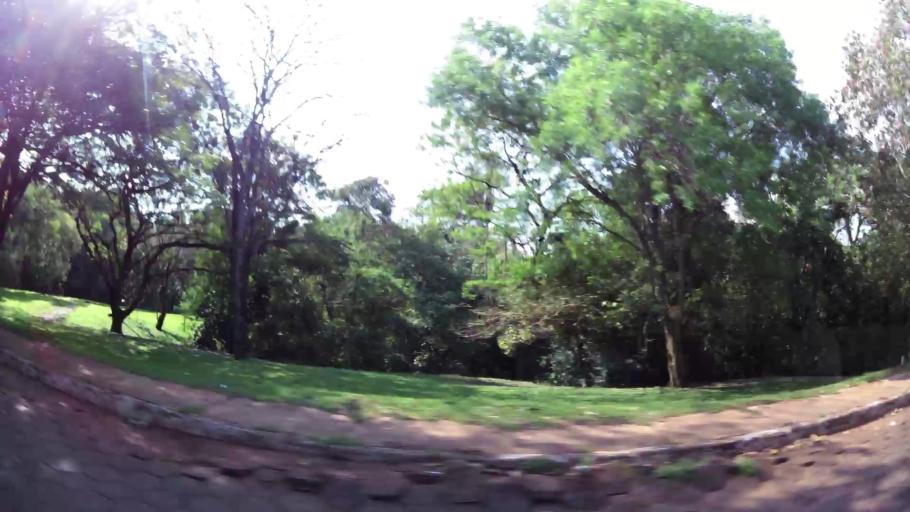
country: PY
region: Alto Parana
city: Ciudad del Este
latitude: -25.5146
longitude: -54.6370
